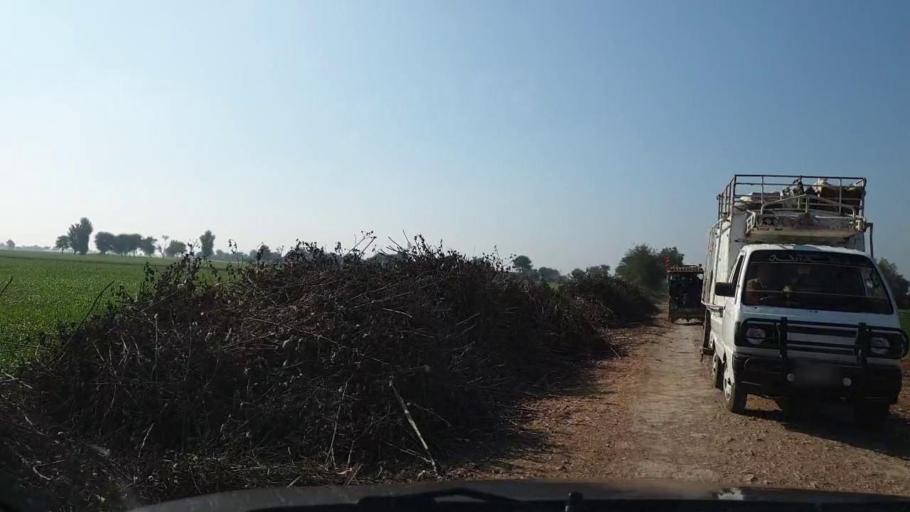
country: PK
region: Sindh
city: Sinjhoro
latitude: 25.9912
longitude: 68.7508
